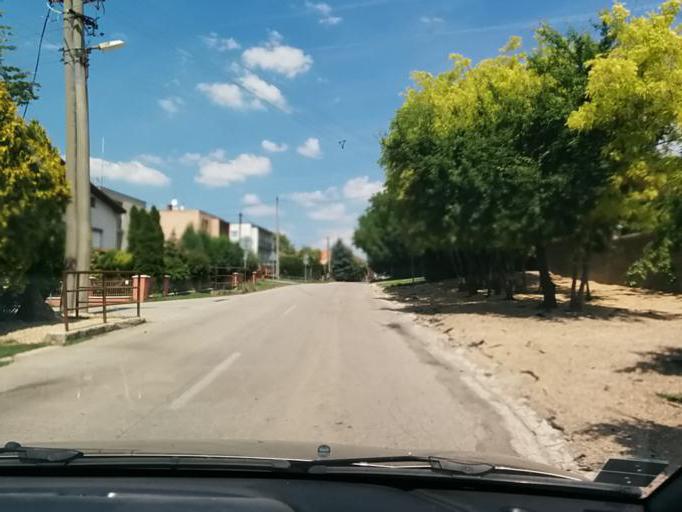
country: SK
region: Trnavsky
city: Sladkovicovo
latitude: 48.2297
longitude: 17.5686
